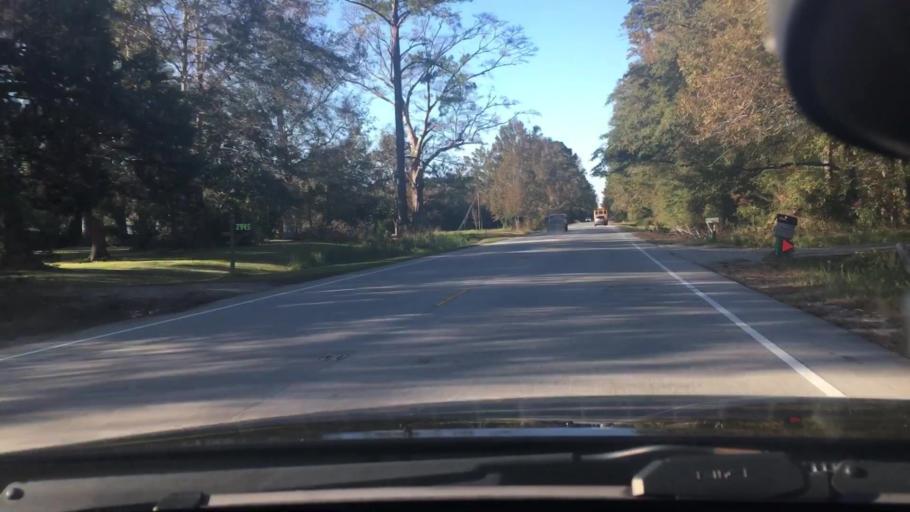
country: US
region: North Carolina
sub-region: Craven County
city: New Bern
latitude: 35.1798
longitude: -77.0472
